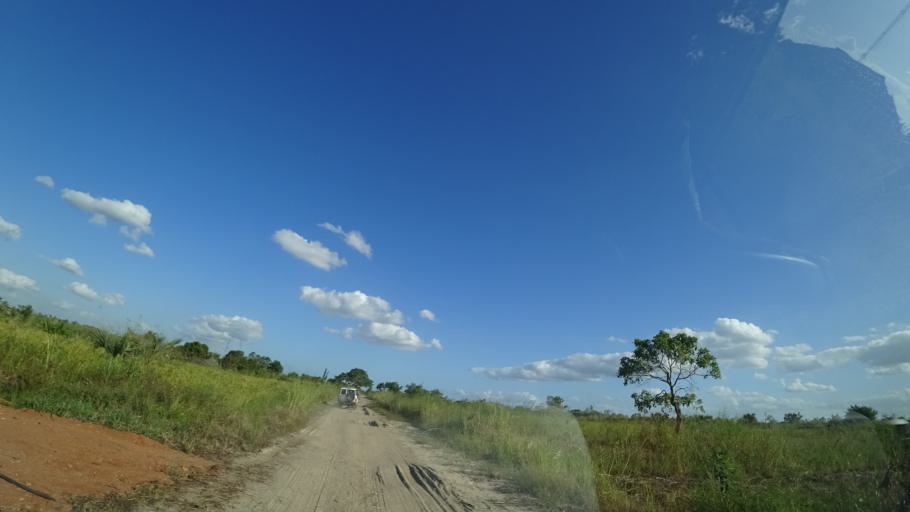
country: MZ
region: Sofala
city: Dondo
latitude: -19.3794
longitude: 34.5921
